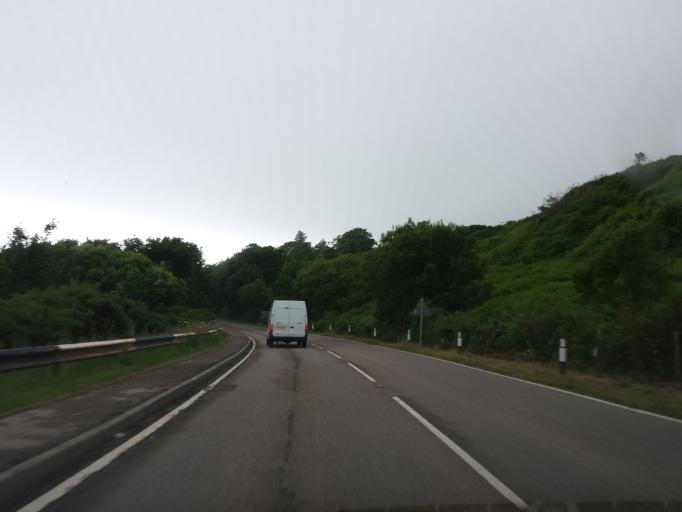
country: GB
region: Scotland
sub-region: Highland
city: Brora
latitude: 58.1131
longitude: -3.6602
